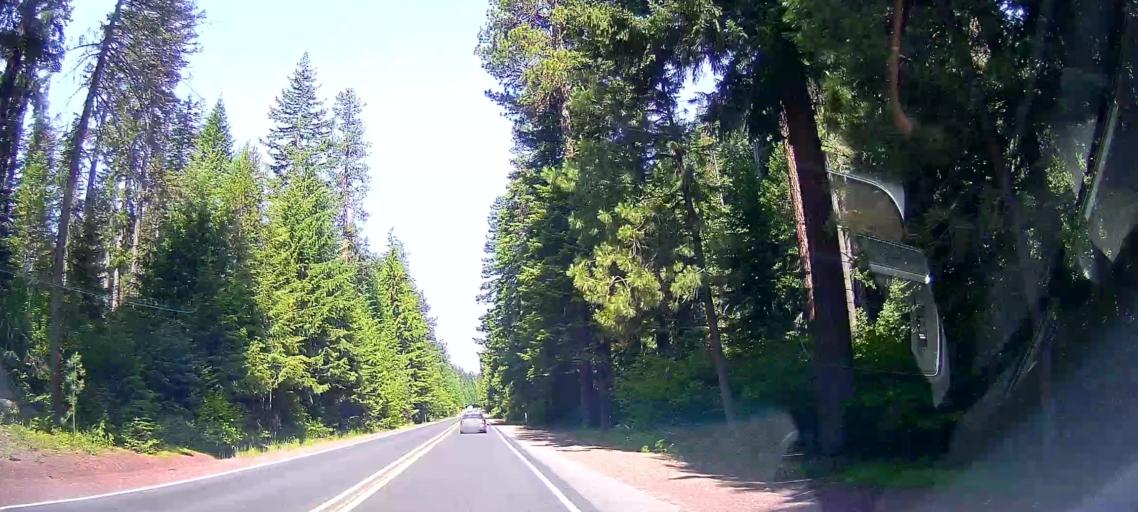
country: US
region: Oregon
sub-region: Jefferson County
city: Warm Springs
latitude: 45.1139
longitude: -121.5697
